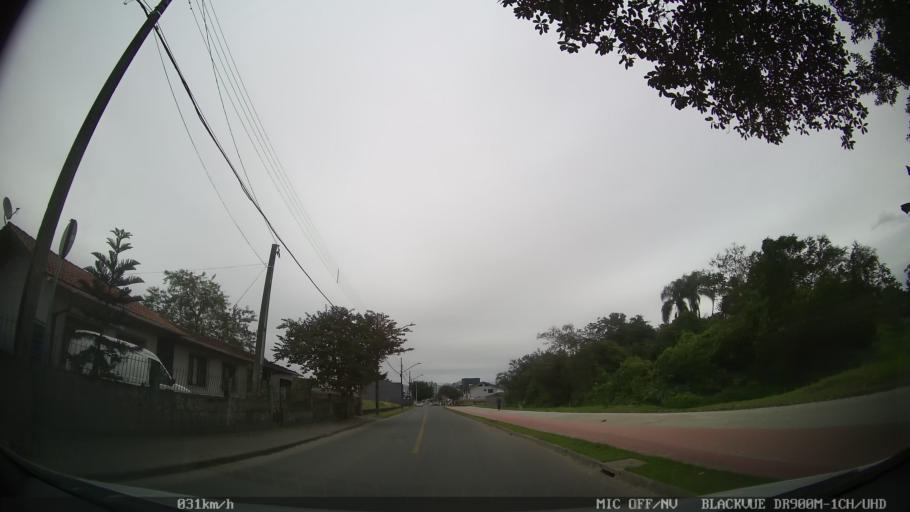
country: BR
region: Santa Catarina
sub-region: Joinville
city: Joinville
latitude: -26.2745
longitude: -48.8409
